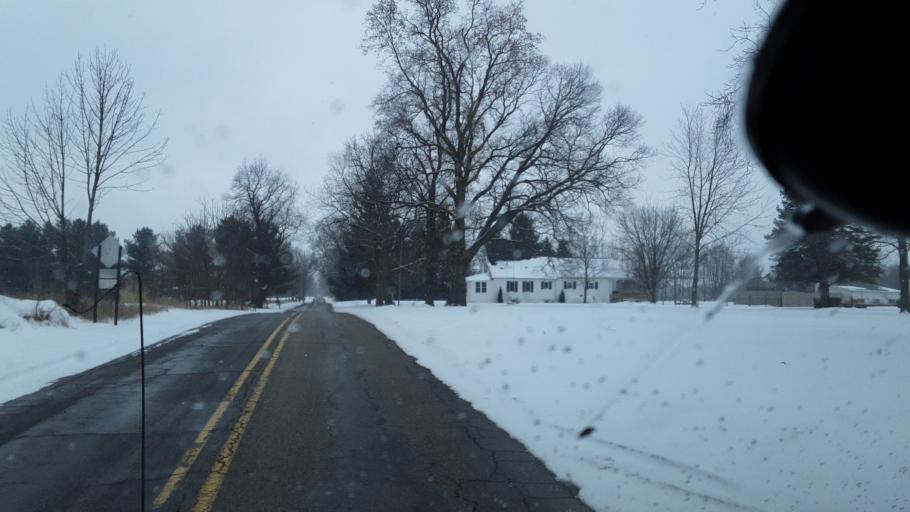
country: US
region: Michigan
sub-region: Ingham County
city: Leslie
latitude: 42.4895
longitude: -84.3942
